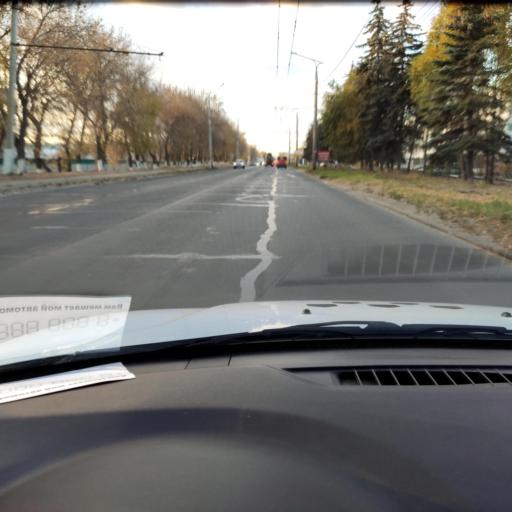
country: RU
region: Samara
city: Tol'yatti
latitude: 53.5382
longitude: 49.4417
